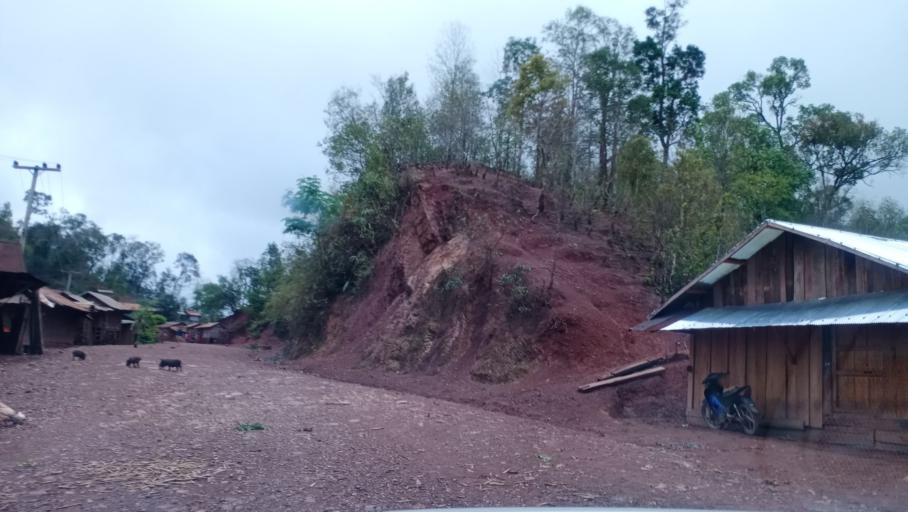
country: LA
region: Phongsali
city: Phongsali
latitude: 21.3380
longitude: 102.0807
